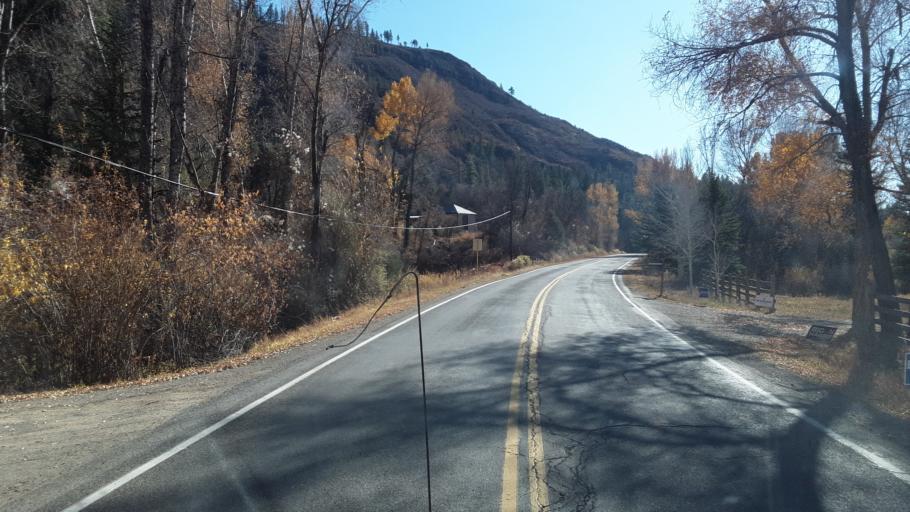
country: US
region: Colorado
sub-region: La Plata County
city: Durango
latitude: 37.4220
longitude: -107.7996
